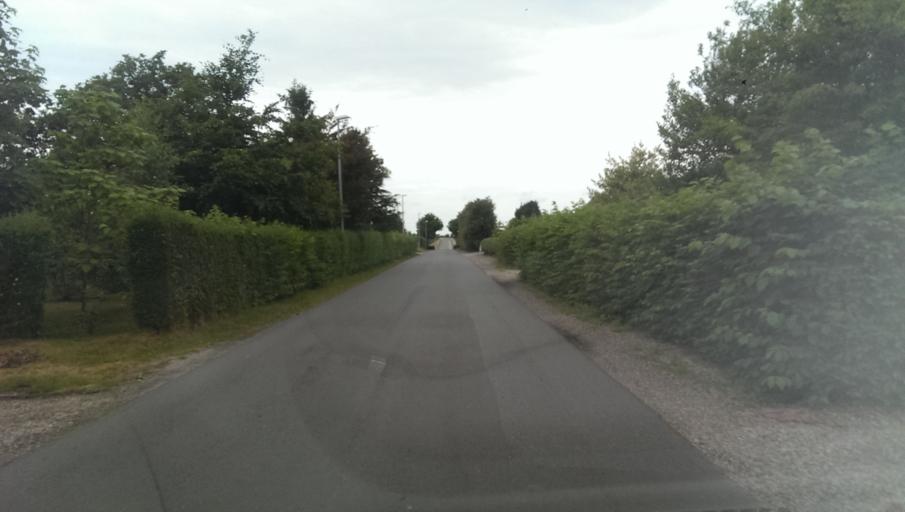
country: DK
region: South Denmark
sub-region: Esbjerg Kommune
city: Bramming
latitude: 55.4324
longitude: 8.6490
